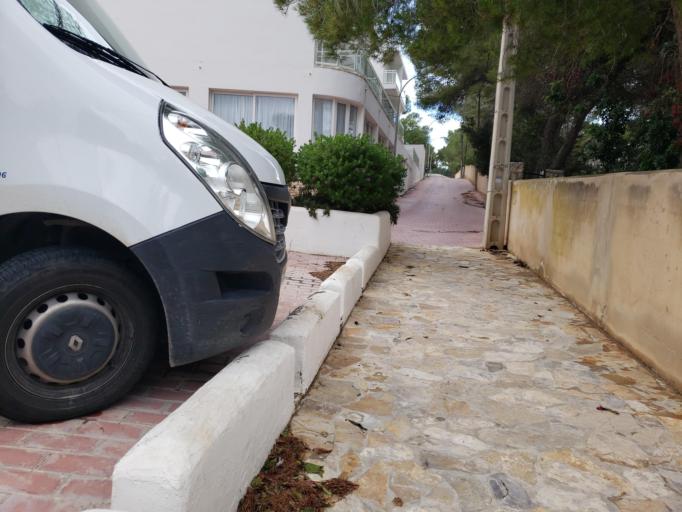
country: ES
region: Balearic Islands
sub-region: Illes Balears
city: Sant Joan de Labritja
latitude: 39.1088
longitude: 1.5147
